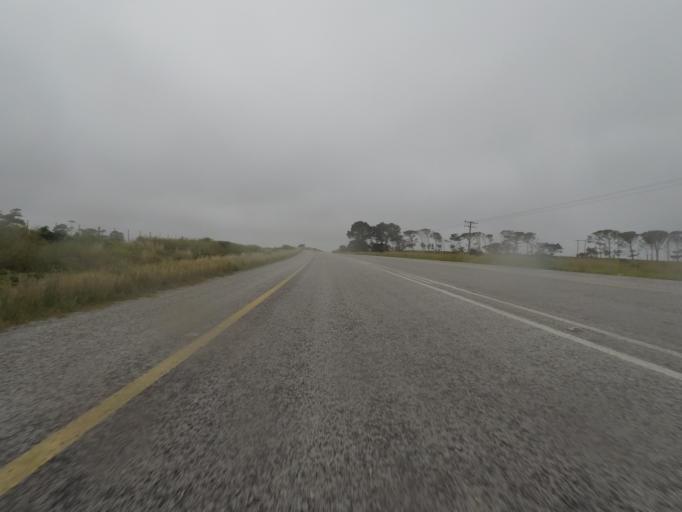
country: ZA
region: Eastern Cape
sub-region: Cacadu District Municipality
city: Grahamstown
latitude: -33.6440
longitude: 26.3465
